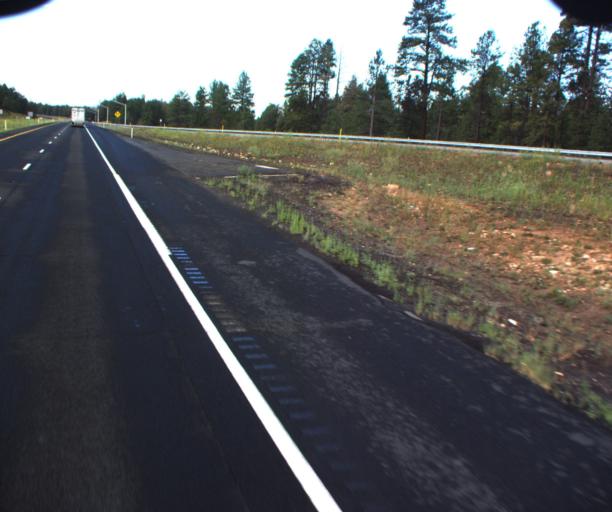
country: US
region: Arizona
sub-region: Coconino County
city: Kachina Village
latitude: 35.1385
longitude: -111.6849
